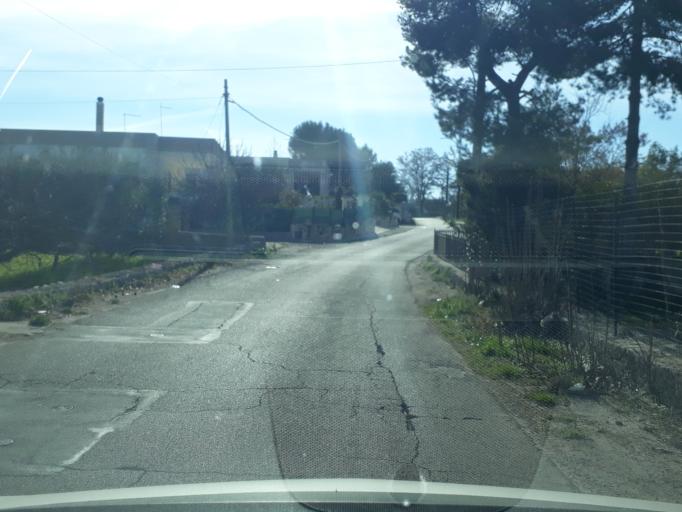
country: IT
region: Apulia
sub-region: Provincia di Brindisi
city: Lamie di Olimpie-Selva
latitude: 40.7953
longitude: 17.3530
